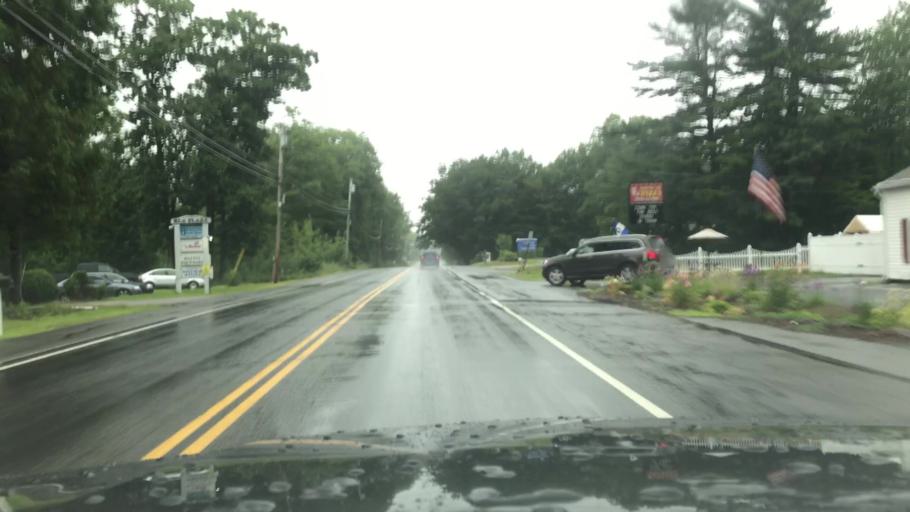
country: US
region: Maine
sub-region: York County
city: Kennebunk
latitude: 43.4145
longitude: -70.5194
